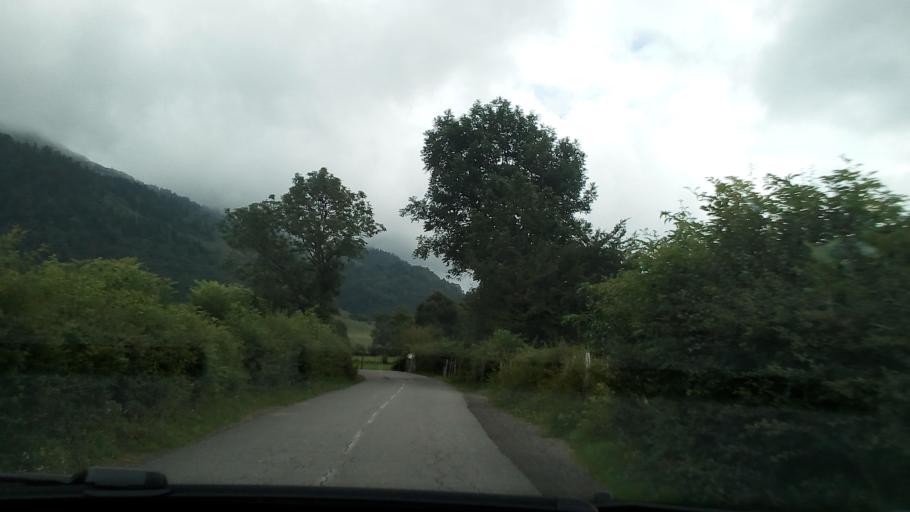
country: FR
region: Aquitaine
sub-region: Departement des Pyrenees-Atlantiques
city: Louvie-Juzon
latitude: 43.0625
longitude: -0.4750
